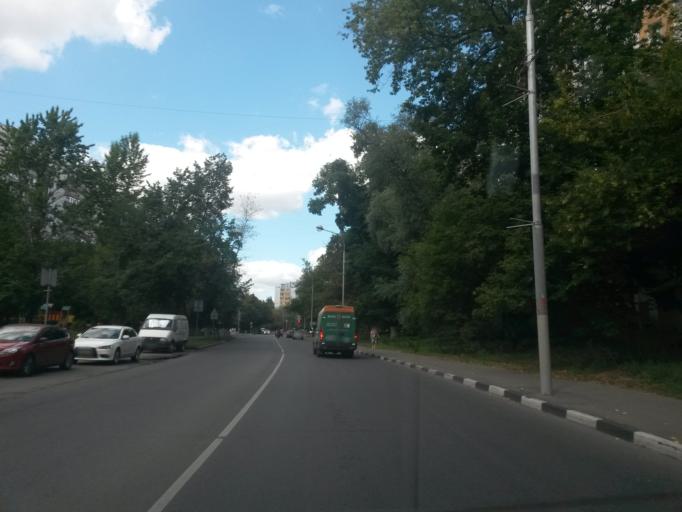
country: RU
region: Moscow
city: Tekstil'shchiki
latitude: 55.6837
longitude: 37.7242
